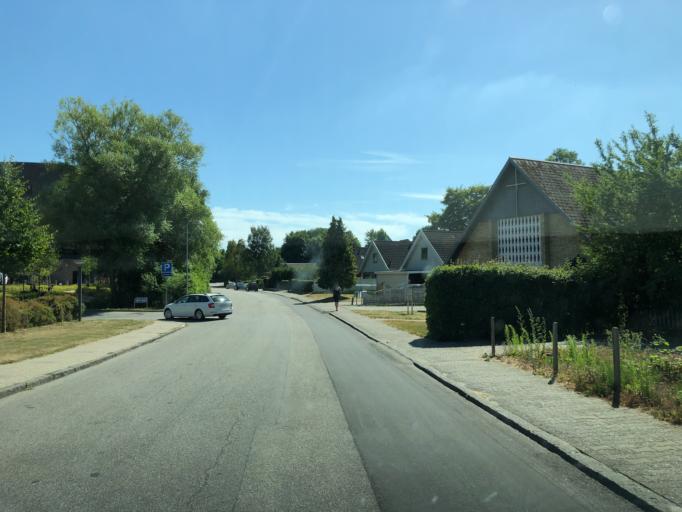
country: DK
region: South Denmark
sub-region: Fredericia Kommune
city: Fredericia
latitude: 55.5687
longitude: 9.7371
